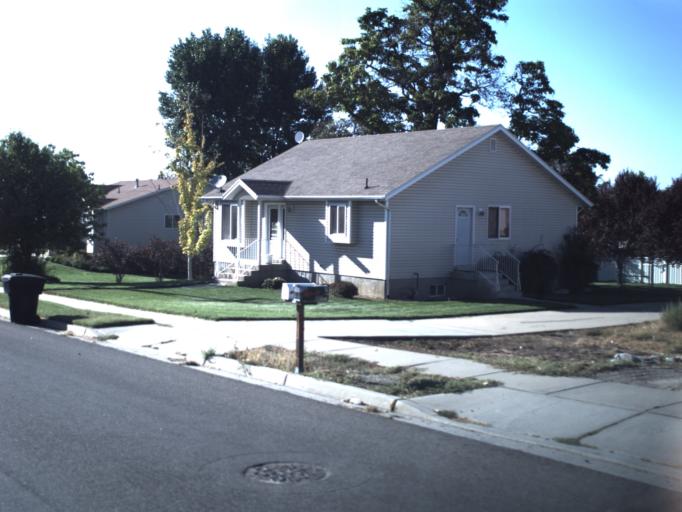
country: US
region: Utah
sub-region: Davis County
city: Sunset
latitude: 41.1399
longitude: -112.0386
